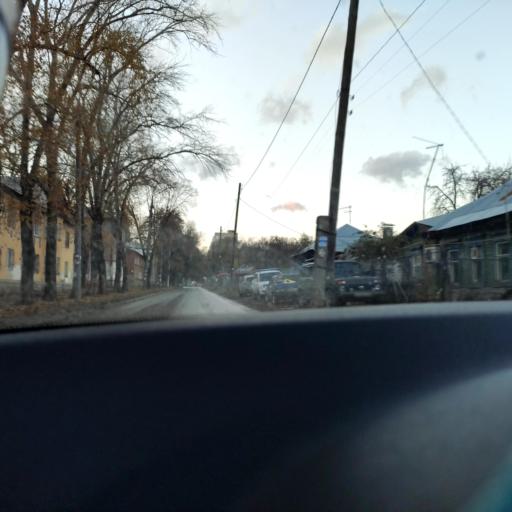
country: RU
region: Samara
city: Samara
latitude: 53.2231
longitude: 50.2474
